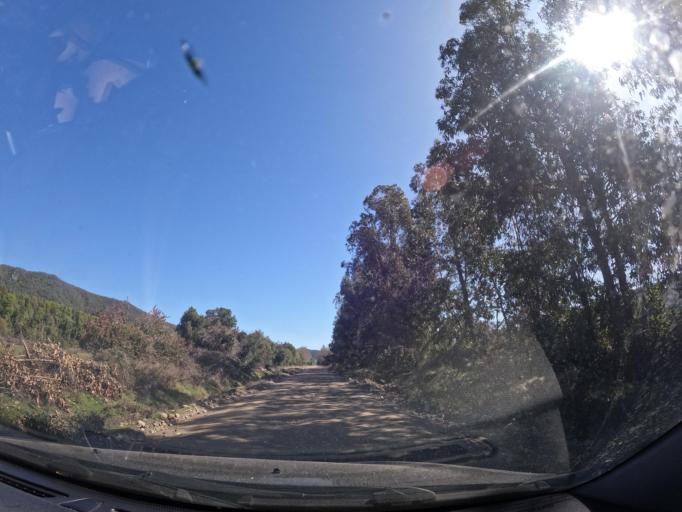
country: CL
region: Maule
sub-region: Provincia de Linares
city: Longavi
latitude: -36.2367
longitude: -71.4190
